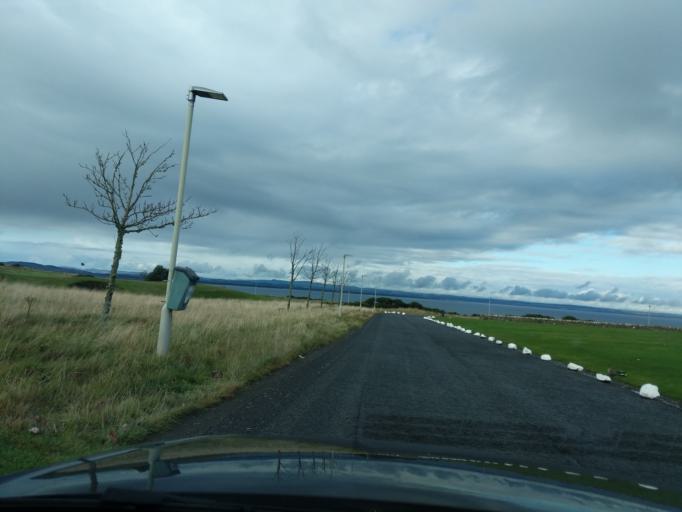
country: GB
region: Scotland
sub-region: Fife
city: Saint Andrews
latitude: 56.3203
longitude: -2.7332
